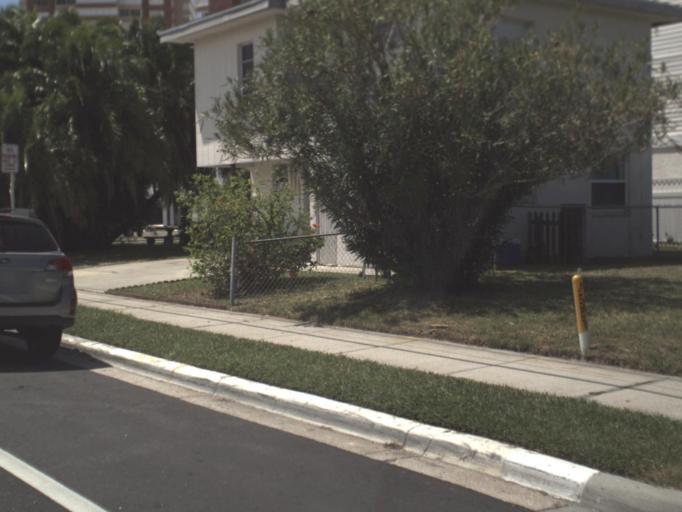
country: US
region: Florida
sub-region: Pinellas County
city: Redington Shores
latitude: 27.8324
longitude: -82.8330
